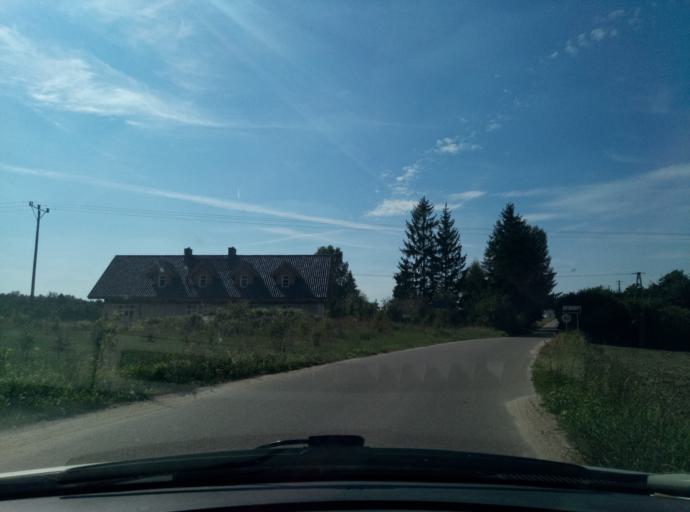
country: PL
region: Kujawsko-Pomorskie
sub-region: Powiat brodnicki
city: Jablonowo Pomorskie
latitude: 53.4123
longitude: 19.2622
